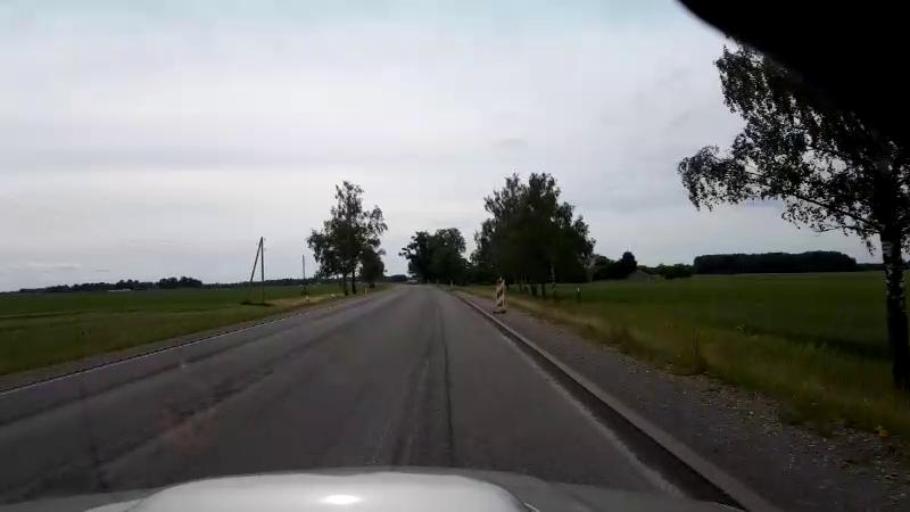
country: LV
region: Bauskas Rajons
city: Bauska
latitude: 56.3408
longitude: 24.2926
